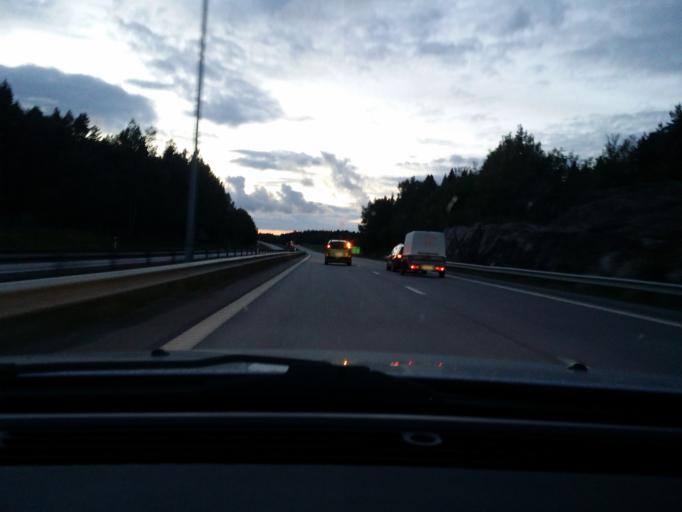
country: SE
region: Stockholm
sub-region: Upplands-Bro Kommun
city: Bro
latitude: 59.5368
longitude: 17.6218
